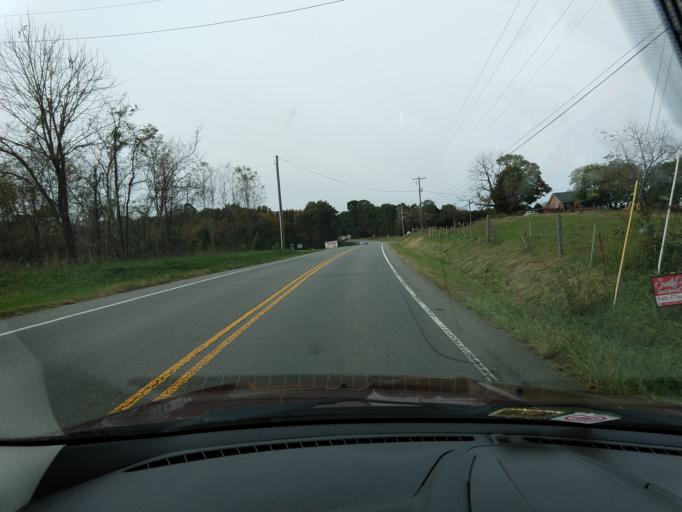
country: US
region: Virginia
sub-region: Franklin County
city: Union Hall
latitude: 36.9945
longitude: -79.7043
